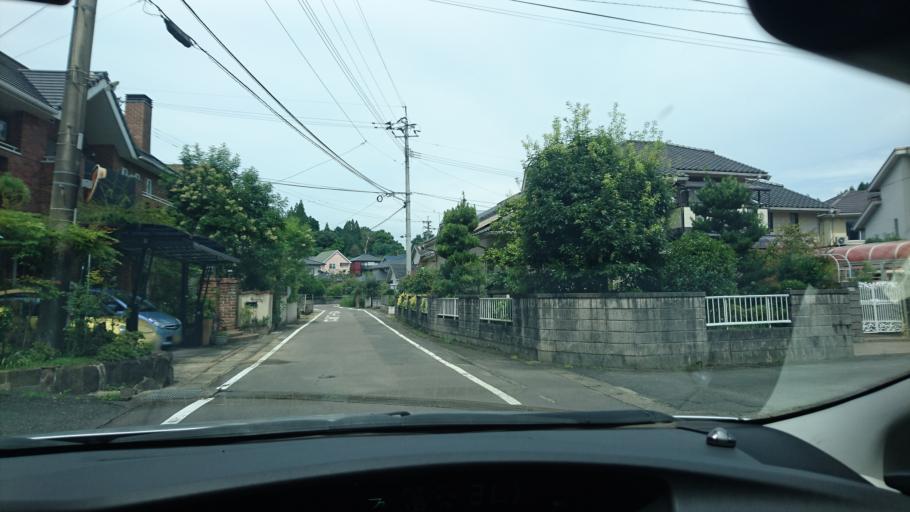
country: JP
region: Saga Prefecture
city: Takeocho-takeo
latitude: 33.2218
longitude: 130.0686
